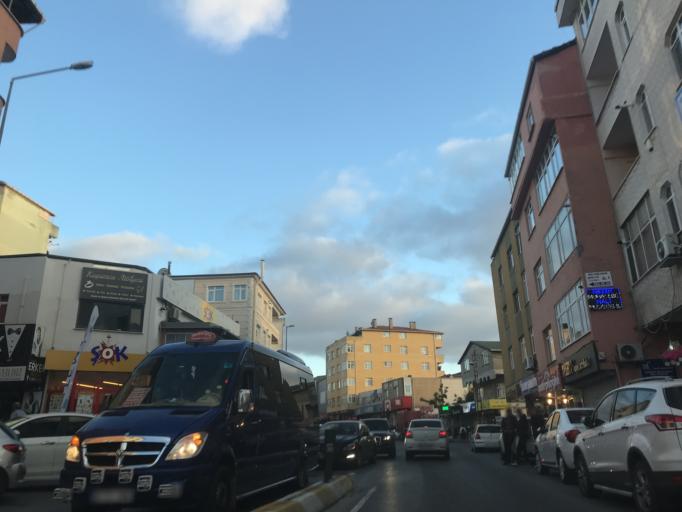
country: TR
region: Istanbul
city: Sisli
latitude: 41.1309
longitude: 29.0412
